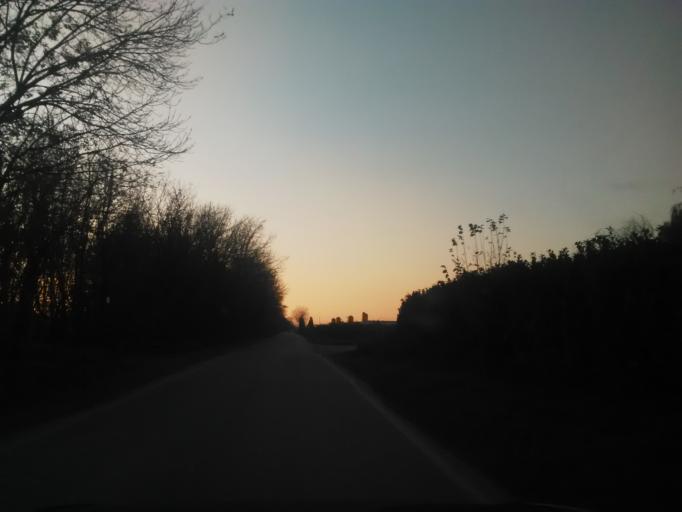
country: IT
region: Piedmont
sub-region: Provincia di Vercelli
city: Santhia
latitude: 45.3603
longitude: 8.1351
